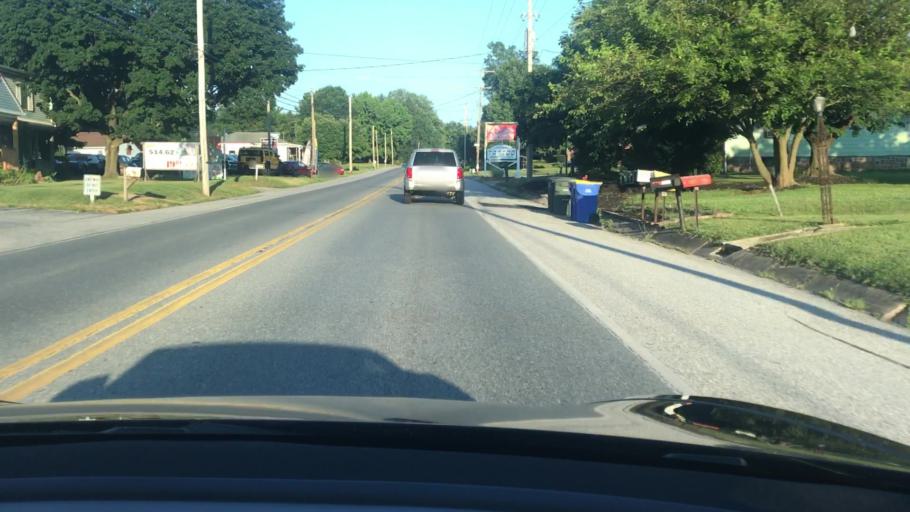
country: US
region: Pennsylvania
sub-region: York County
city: Weigelstown
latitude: 39.9884
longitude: -76.8350
